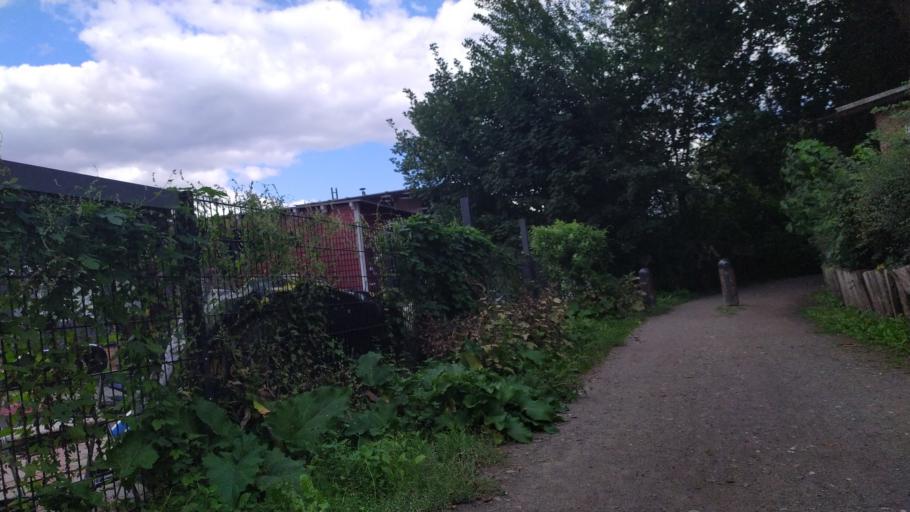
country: DE
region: Berlin
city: Berlin Koepenick
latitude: 52.4490
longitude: 13.6013
